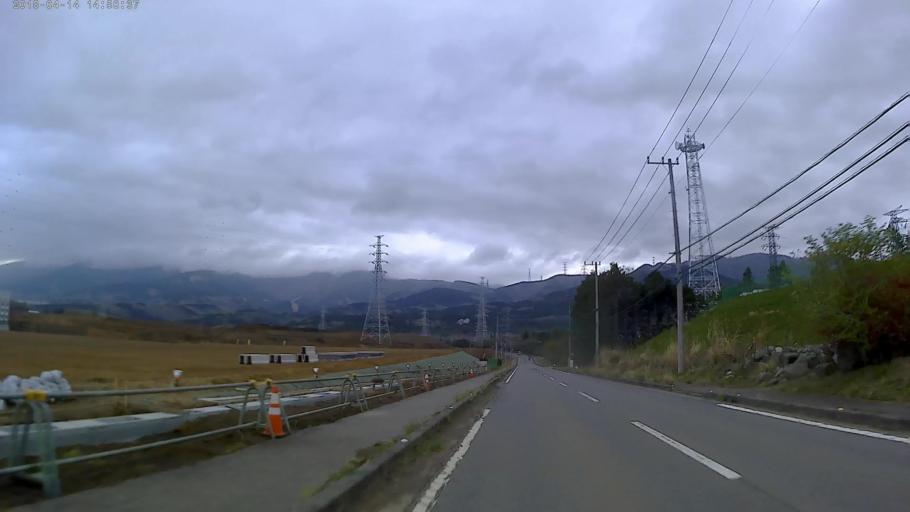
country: JP
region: Shizuoka
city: Gotemba
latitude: 35.3674
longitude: 138.9654
